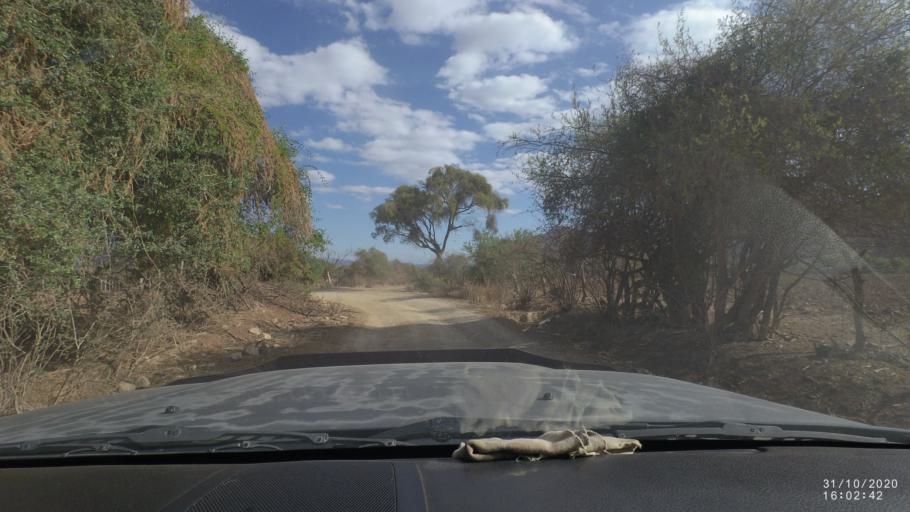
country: BO
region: Chuquisaca
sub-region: Provincia Zudanez
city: Mojocoya
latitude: -18.3485
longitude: -64.6562
